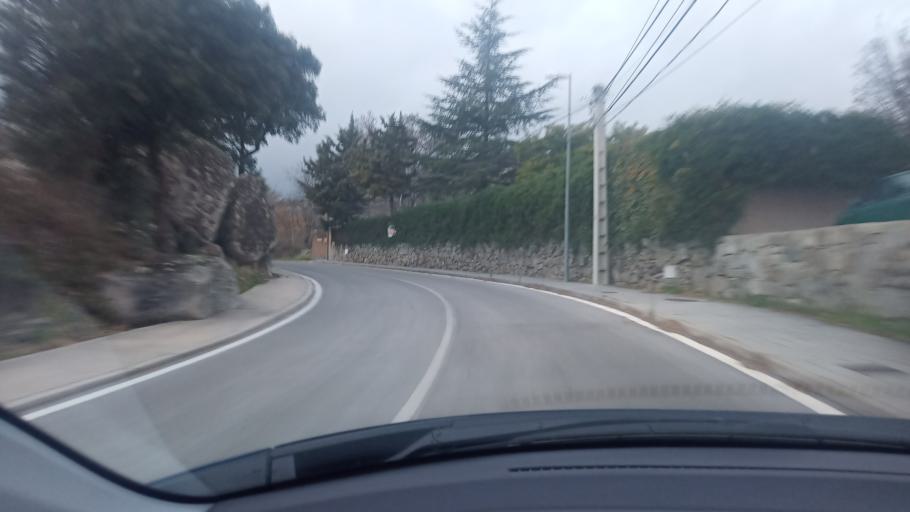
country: ES
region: Madrid
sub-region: Provincia de Madrid
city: Zarzalejo
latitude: 40.5424
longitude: -4.1711
